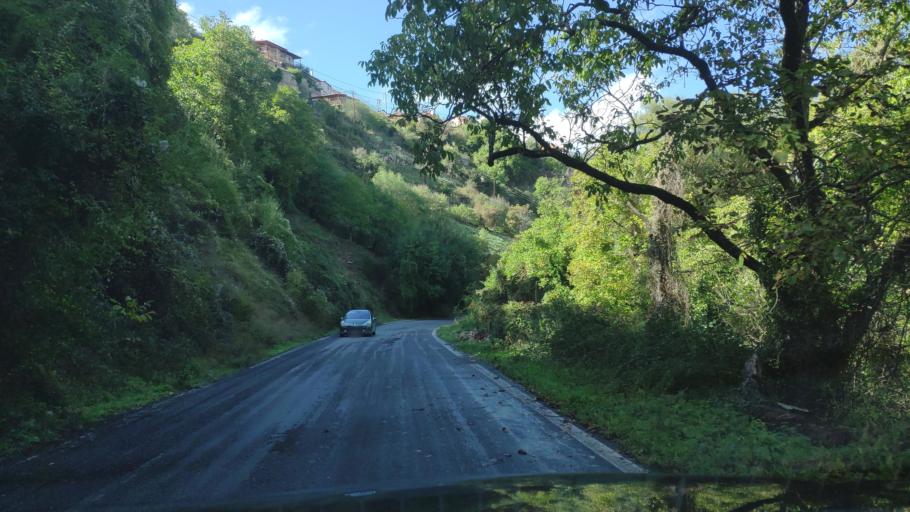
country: GR
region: Peloponnese
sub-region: Nomos Arkadias
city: Dimitsana
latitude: 37.5963
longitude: 22.0401
